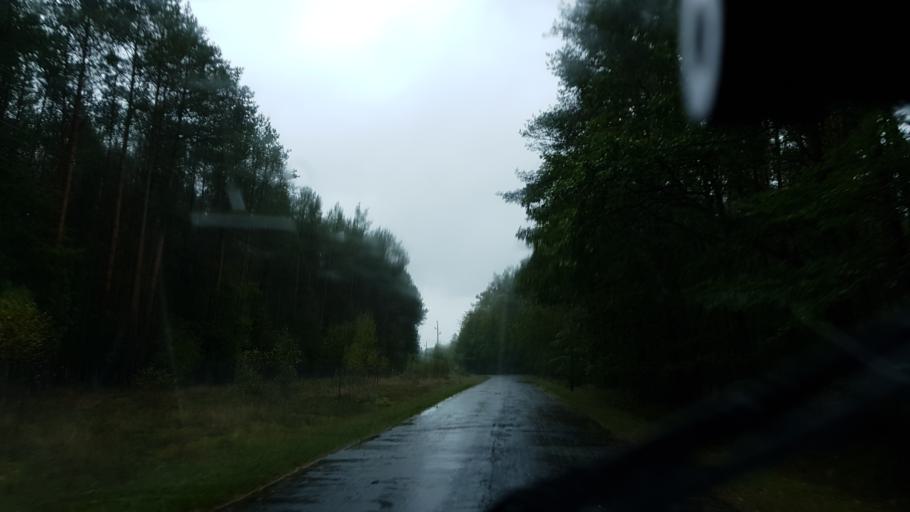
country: PL
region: West Pomeranian Voivodeship
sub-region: Powiat goleniowski
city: Przybiernow
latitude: 53.6732
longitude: 14.7309
